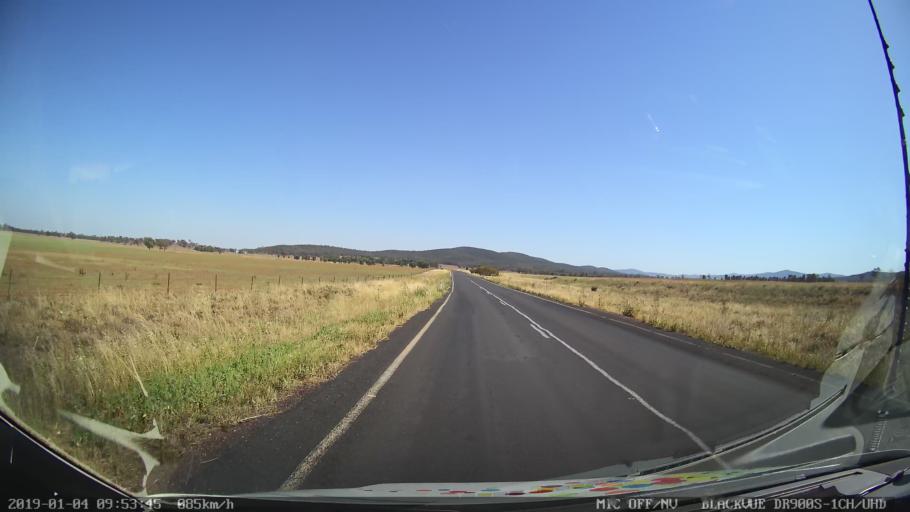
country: AU
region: New South Wales
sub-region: Cabonne
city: Canowindra
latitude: -33.5484
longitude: 148.4198
